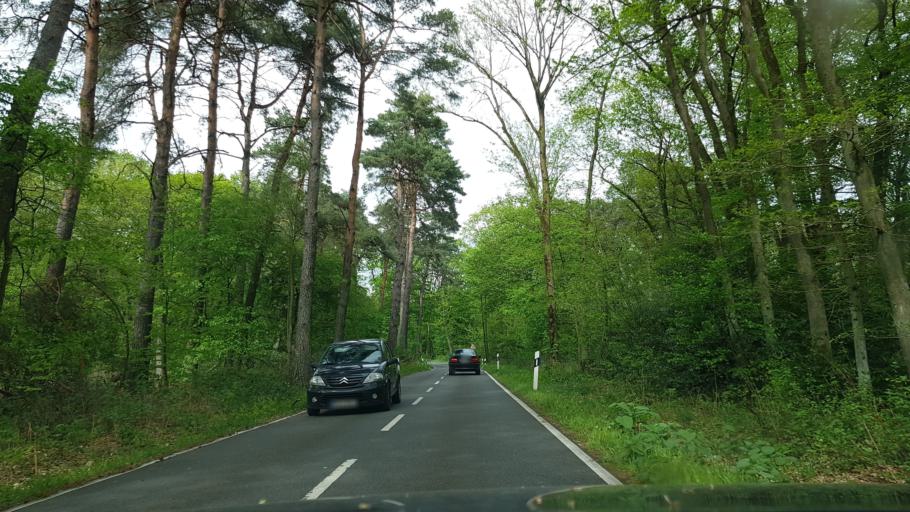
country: DE
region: North Rhine-Westphalia
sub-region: Regierungsbezirk Dusseldorf
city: Muelheim (Ruhr)
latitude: 51.3893
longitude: 6.8325
